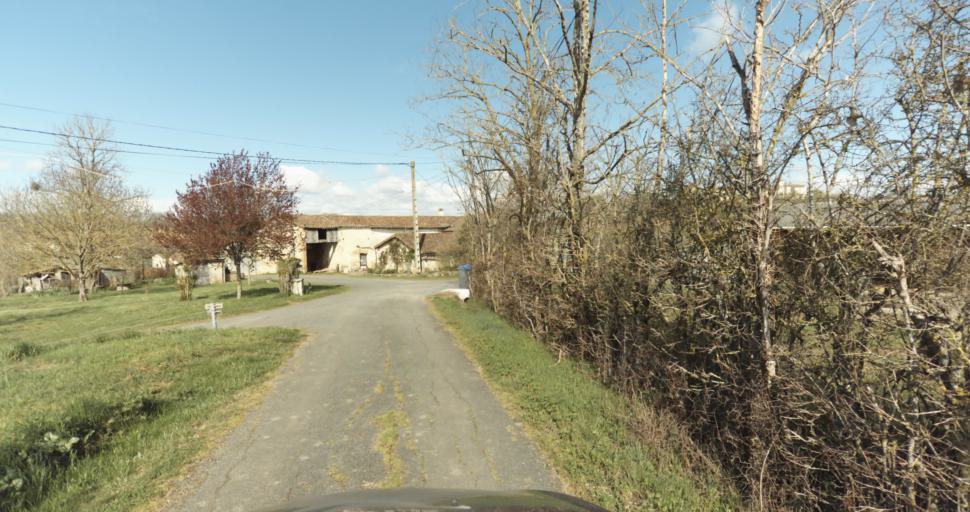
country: FR
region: Midi-Pyrenees
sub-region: Departement du Tarn
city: Frejairolles
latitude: 43.8629
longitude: 2.1919
